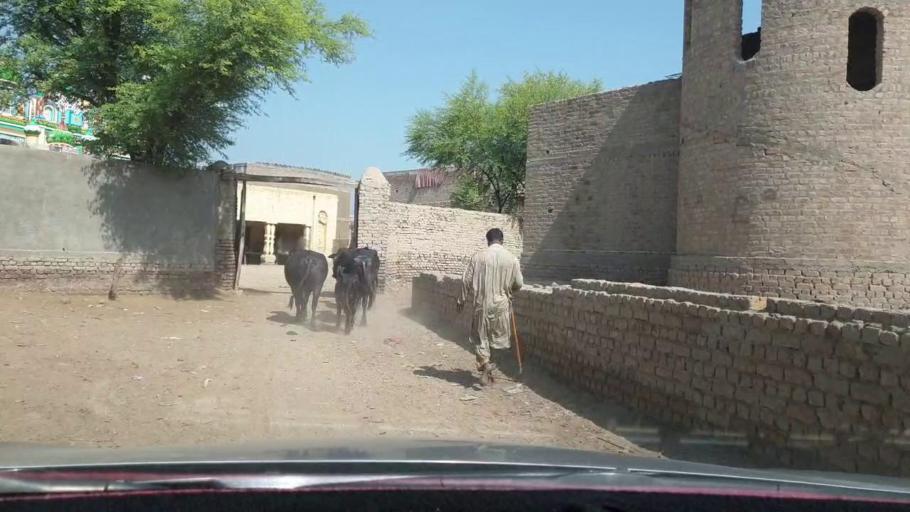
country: PK
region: Sindh
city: Kambar
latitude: 27.5994
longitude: 67.9730
